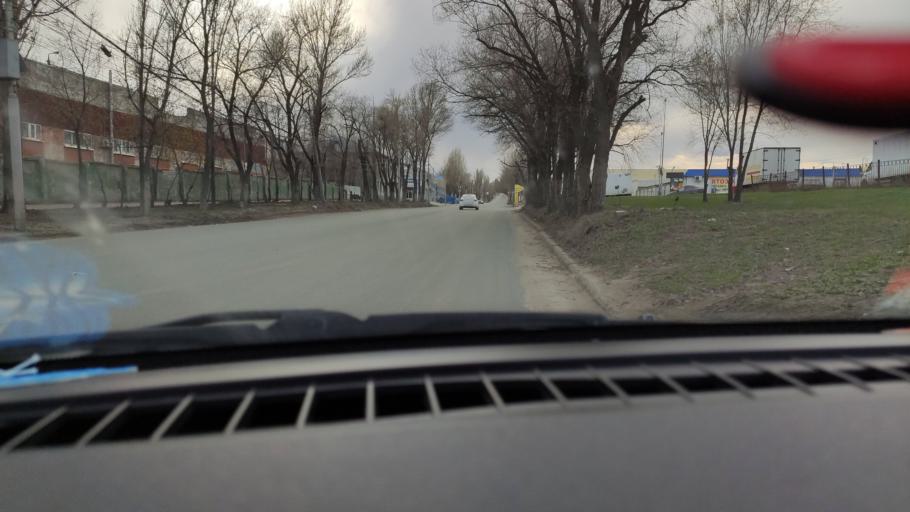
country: RU
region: Saratov
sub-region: Saratovskiy Rayon
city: Saratov
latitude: 51.6151
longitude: 45.9661
